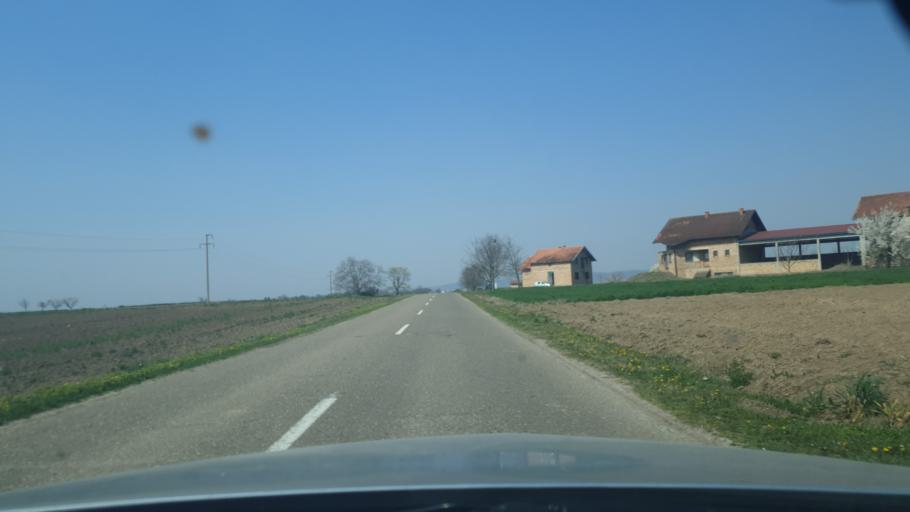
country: RS
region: Autonomna Pokrajina Vojvodina
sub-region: Sremski Okrug
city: Ruma
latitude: 45.0127
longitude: 19.7812
